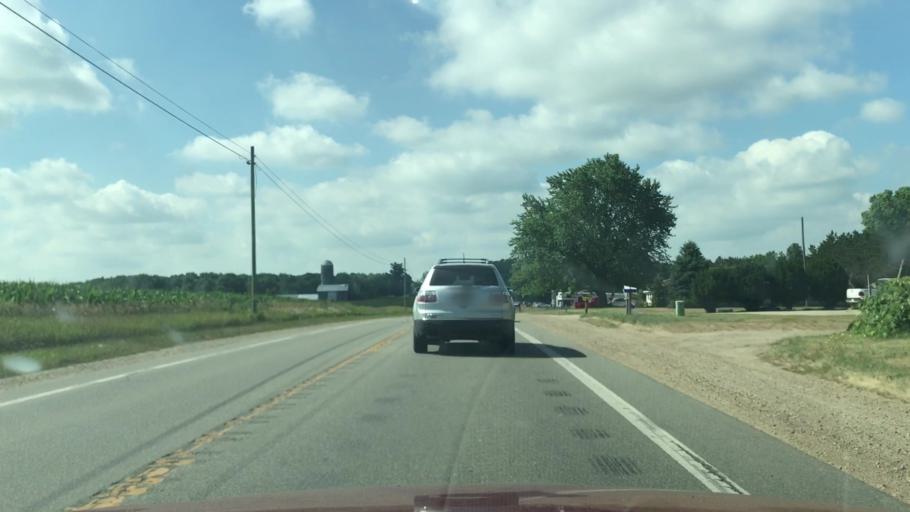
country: US
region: Michigan
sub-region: Kent County
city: Kent City
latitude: 43.2991
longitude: -85.8106
